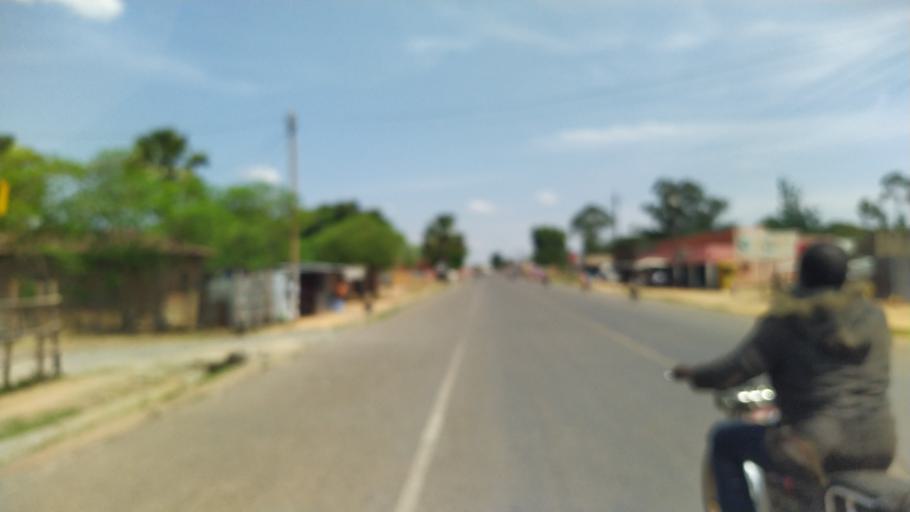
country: UG
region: Northern Region
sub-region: Arua District
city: Arua
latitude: 3.0345
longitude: 30.9133
